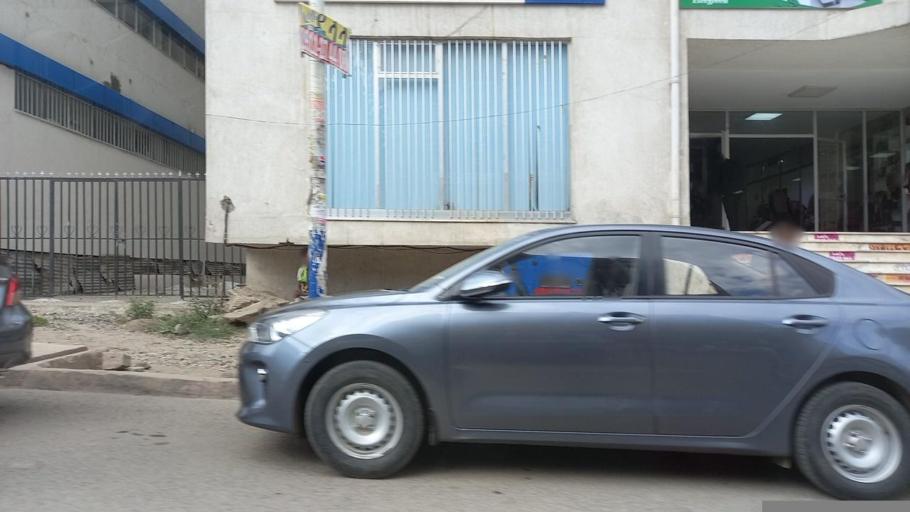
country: ET
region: Adis Abeba
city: Addis Ababa
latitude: 9.0101
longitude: 38.8506
